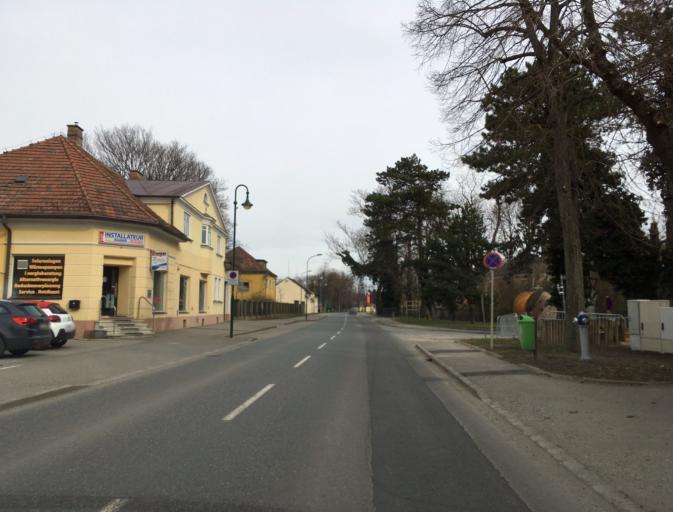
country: AT
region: Lower Austria
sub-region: Politischer Bezirk Ganserndorf
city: Leopoldsdorf im Marchfelde
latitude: 48.2255
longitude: 16.6924
